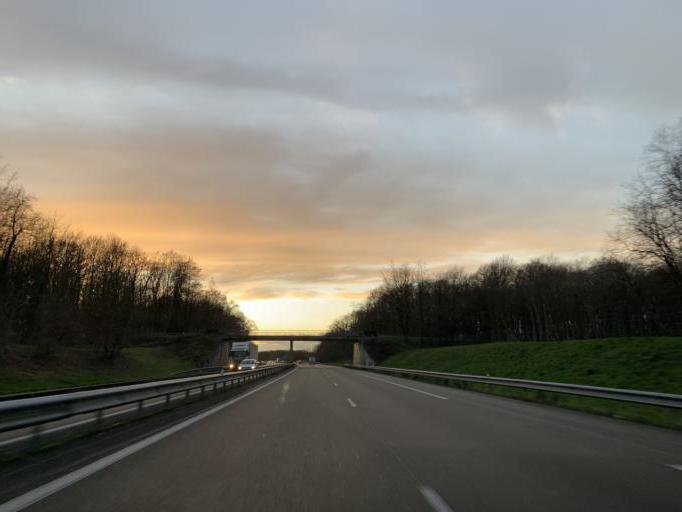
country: FR
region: Champagne-Ardenne
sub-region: Departement de l'Aube
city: Bar-sur-Seine
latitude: 48.1827
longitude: 4.3925
